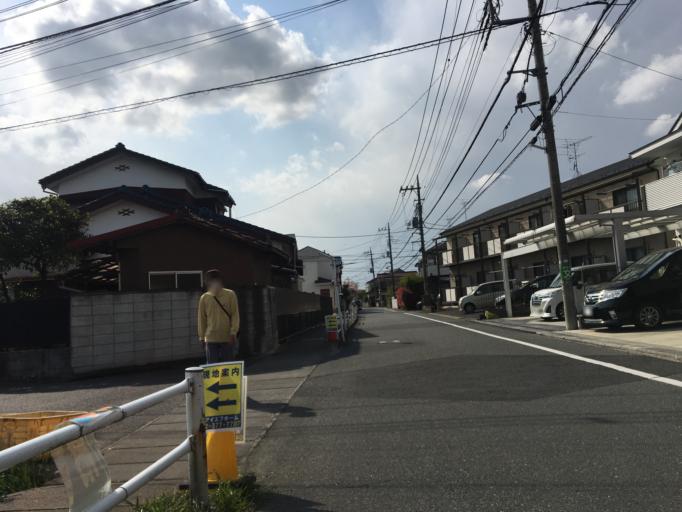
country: JP
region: Tokyo
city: Chofugaoka
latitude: 35.6443
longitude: 139.5085
